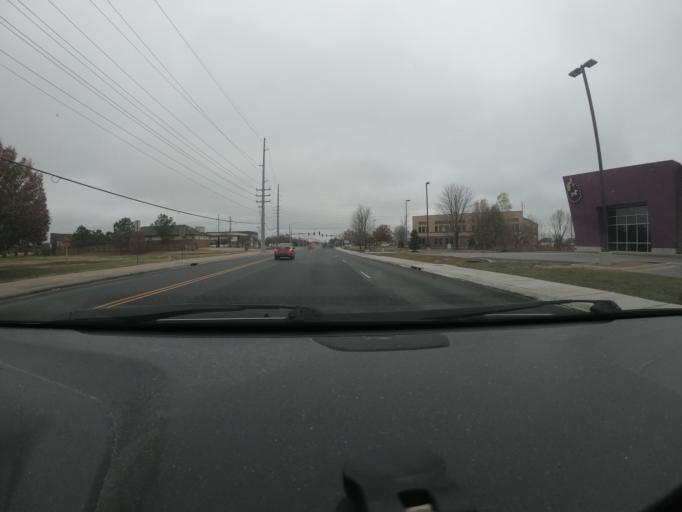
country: US
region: Arkansas
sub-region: Benton County
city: Bentonville
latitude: 36.3590
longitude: -94.2220
